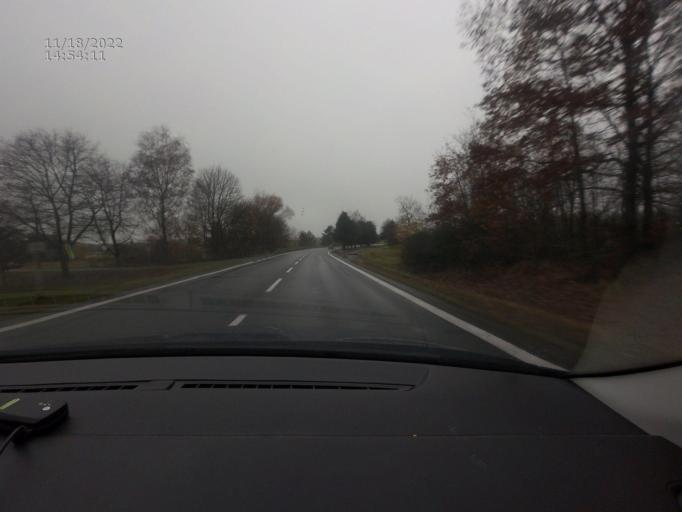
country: CZ
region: Jihocesky
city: Milevsko
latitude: 49.4607
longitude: 14.3342
